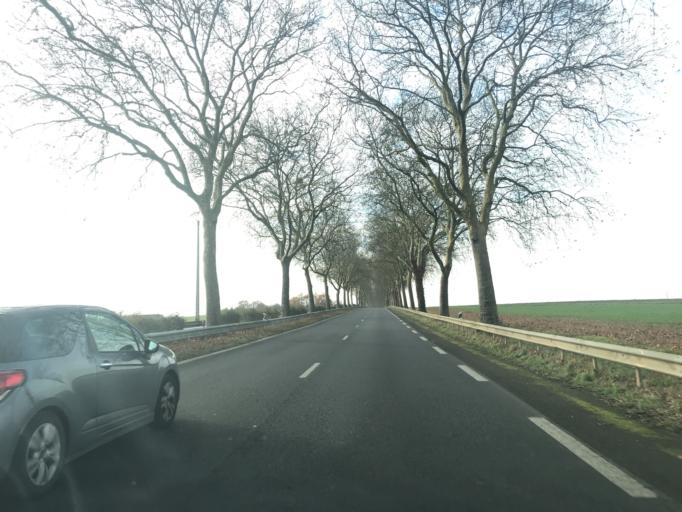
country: FR
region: Poitou-Charentes
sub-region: Departement des Deux-Sevres
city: Chauray
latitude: 46.3486
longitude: -0.3506
